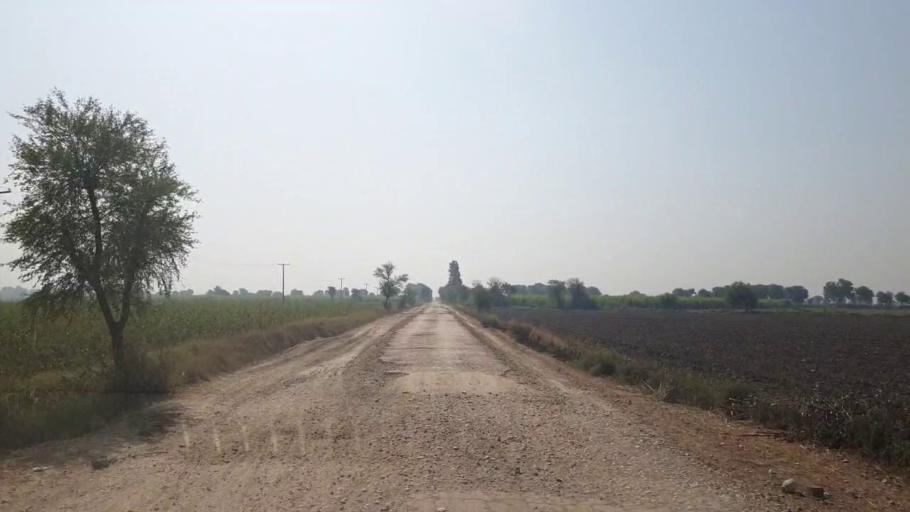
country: PK
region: Sindh
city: Shahdadpur
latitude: 25.9120
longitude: 68.7409
